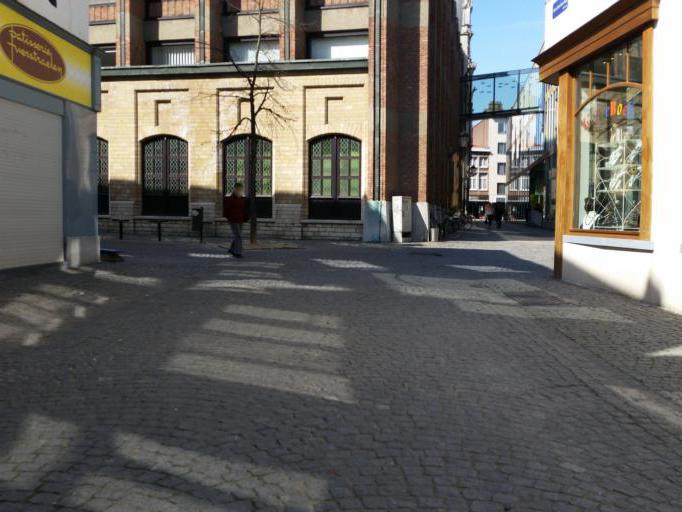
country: BE
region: Flanders
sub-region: Provincie Antwerpen
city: Mechelen
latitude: 51.0273
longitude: 4.4822
